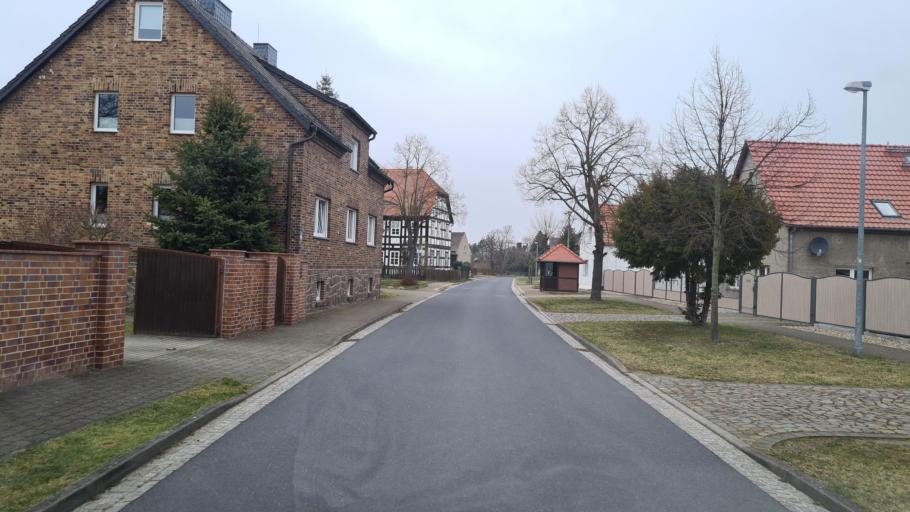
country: DE
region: Brandenburg
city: Herzberg
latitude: 51.6476
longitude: 13.1891
